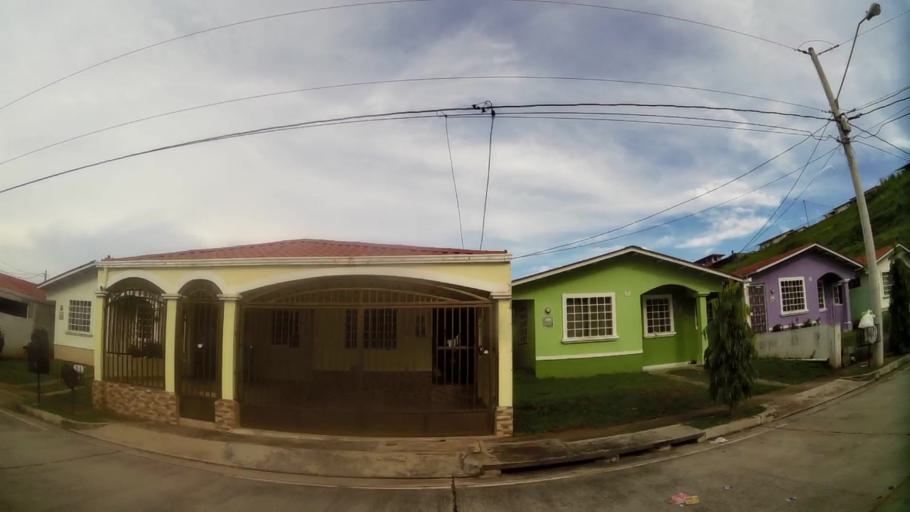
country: PA
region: Panama
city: La Chorrera
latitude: 8.8812
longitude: -79.7686
